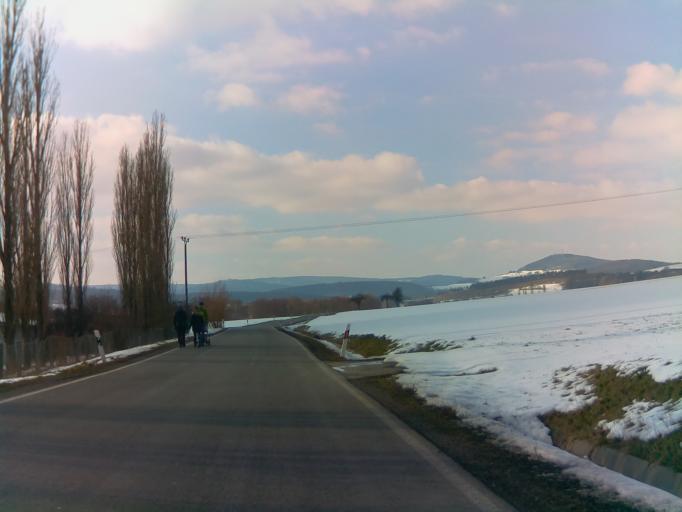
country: DE
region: Thuringia
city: Oberkatz
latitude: 50.5653
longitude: 10.2309
